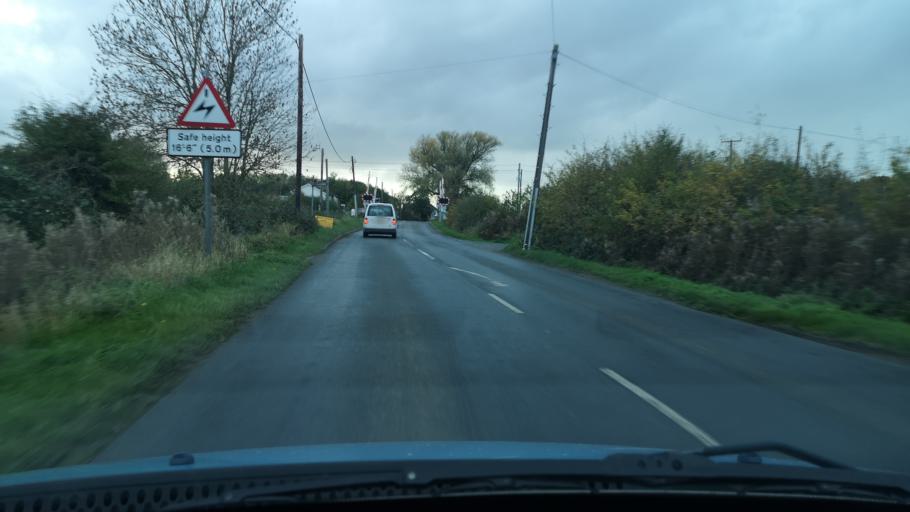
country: GB
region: England
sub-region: Doncaster
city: Moss
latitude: 53.6225
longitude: -1.1113
